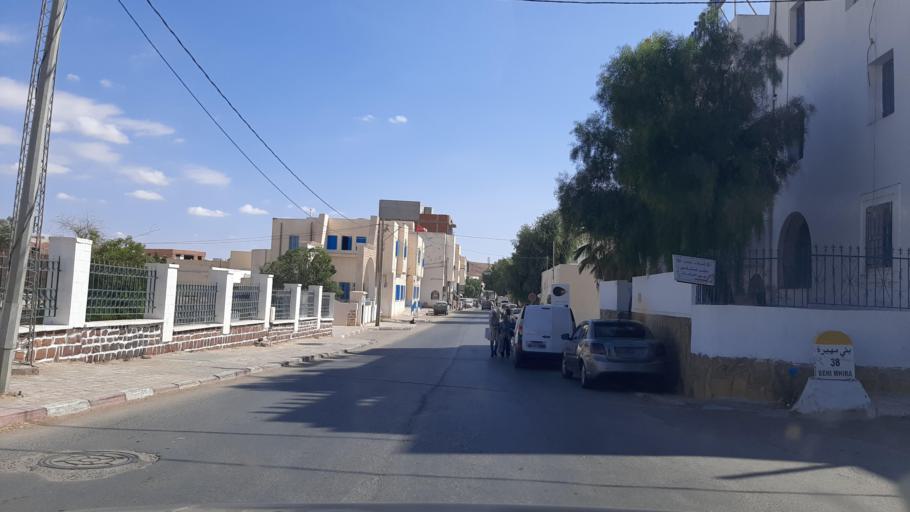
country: TN
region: Tataouine
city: Tataouine
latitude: 32.9265
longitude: 10.4449
